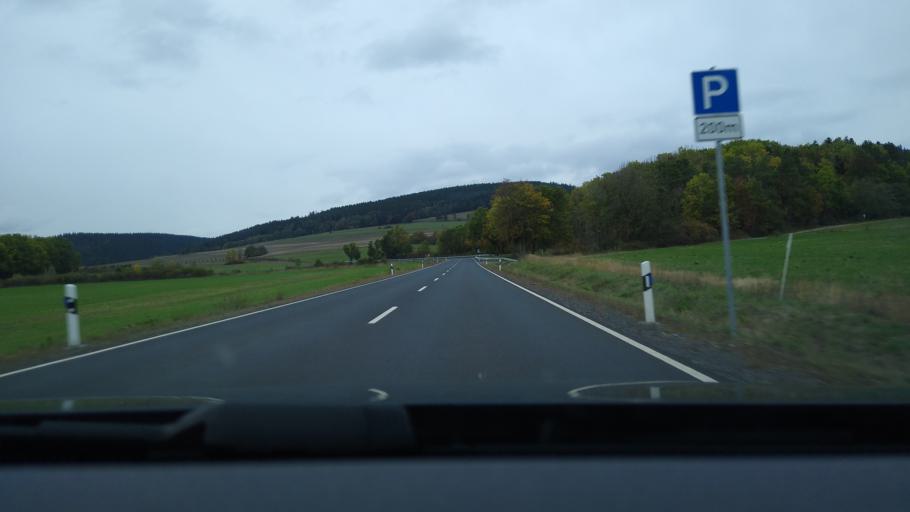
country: DE
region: Thuringia
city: Eisfeld
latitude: 50.4482
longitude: 10.9372
